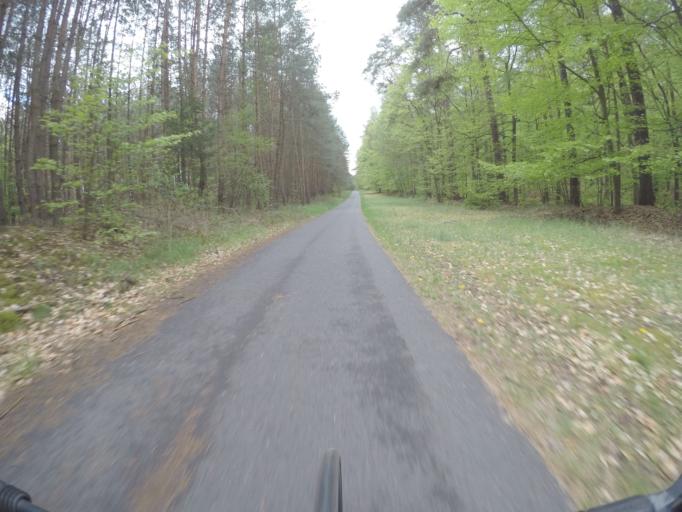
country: DE
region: Brandenburg
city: Biesenthal
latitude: 52.7995
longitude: 13.6252
